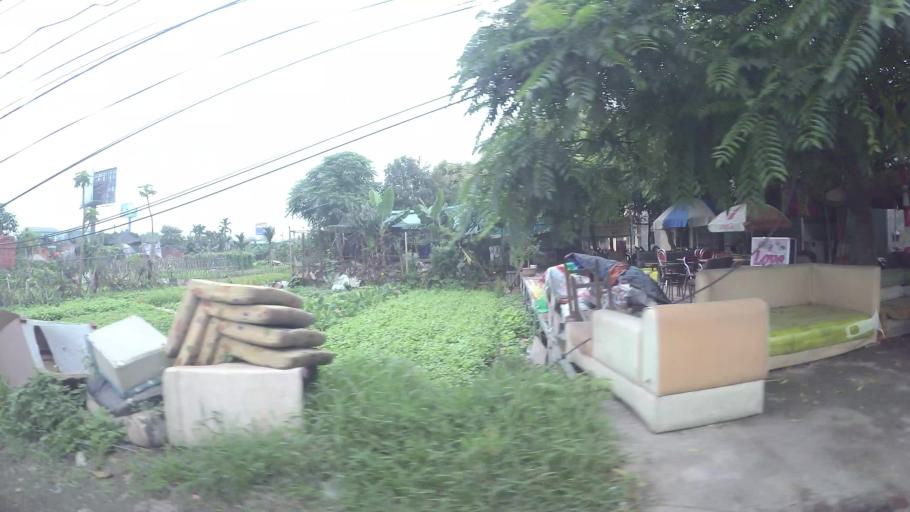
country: VN
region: Ha Noi
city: Hai BaTrung
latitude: 20.9840
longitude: 105.8908
